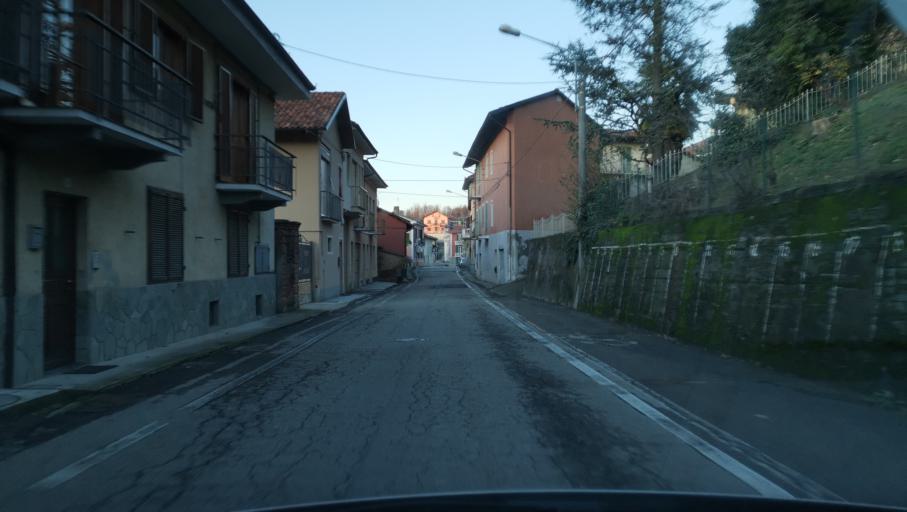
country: IT
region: Piedmont
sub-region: Provincia di Asti
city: Berzano di San Pietro
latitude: 45.0933
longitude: 7.9528
